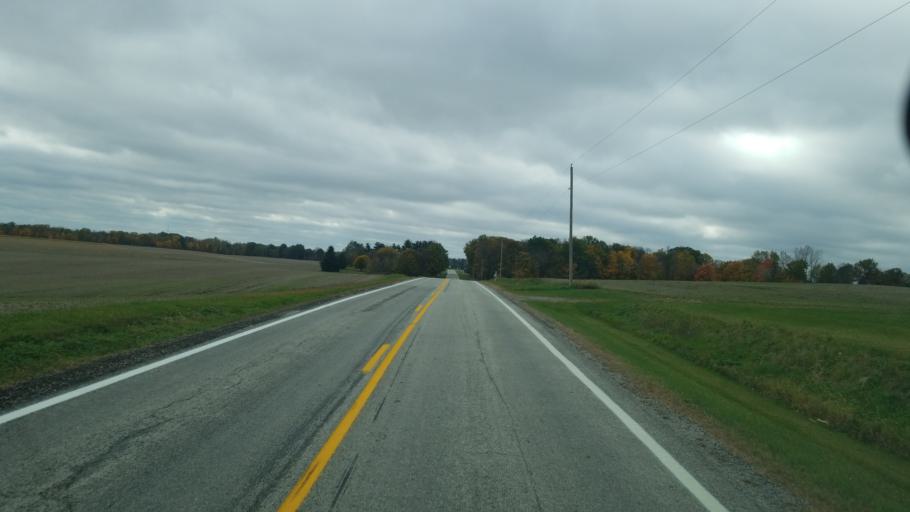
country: US
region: Ohio
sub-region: Crawford County
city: Crestline
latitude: 40.8769
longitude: -82.7666
